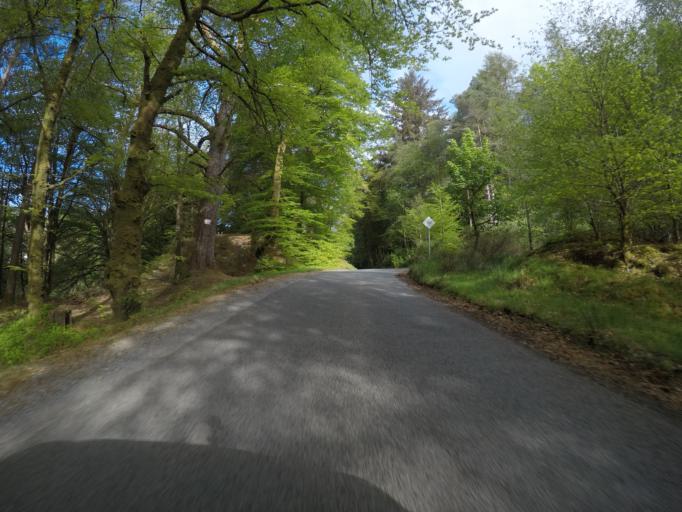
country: GB
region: Scotland
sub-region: Highland
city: Fort William
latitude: 56.6825
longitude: -5.0931
